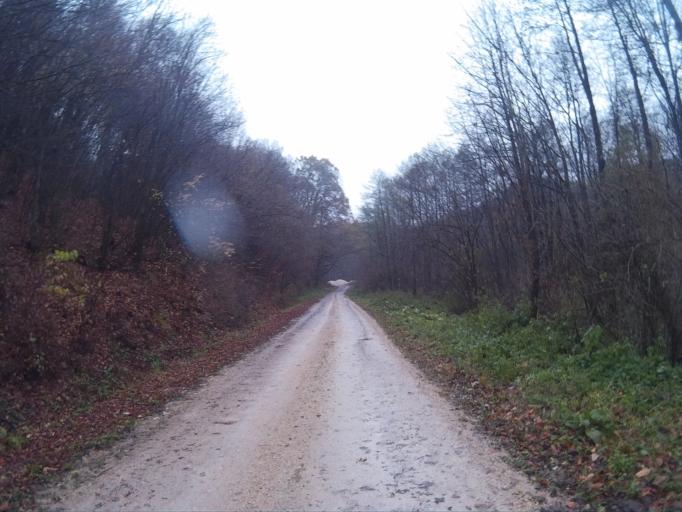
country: HU
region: Veszprem
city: Herend
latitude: 47.2331
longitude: 17.7366
